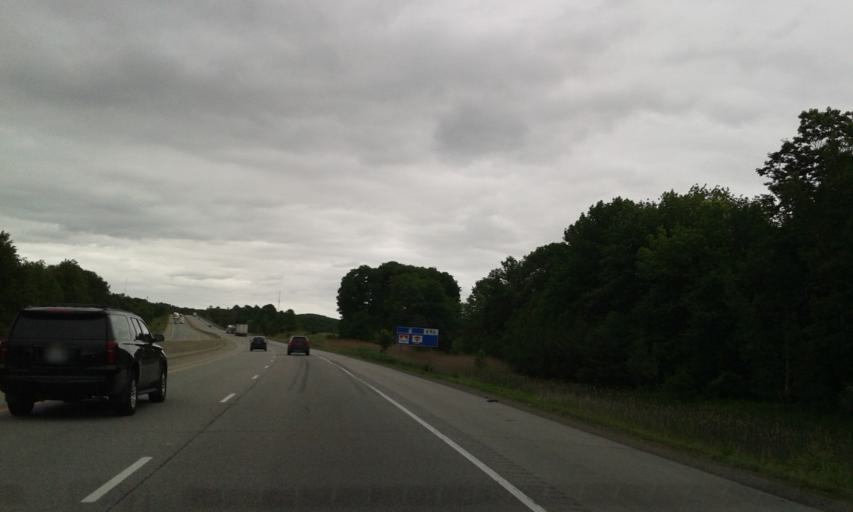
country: CA
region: Ontario
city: Brockville
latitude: 44.5686
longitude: -75.7395
